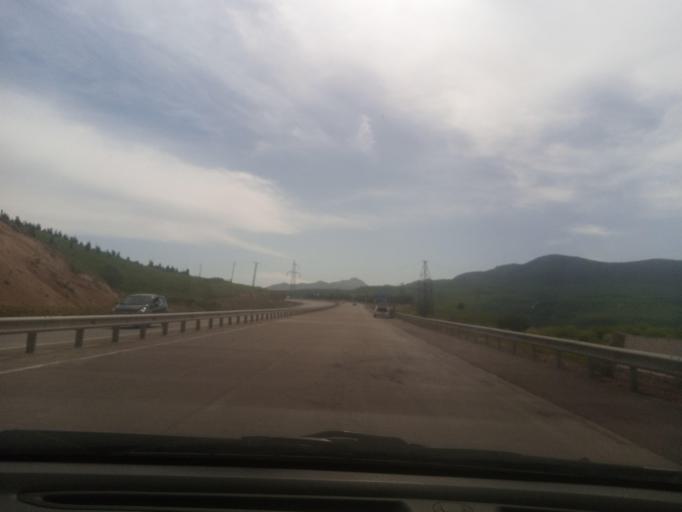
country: UZ
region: Toshkent
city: Angren
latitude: 41.0673
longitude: 70.2233
